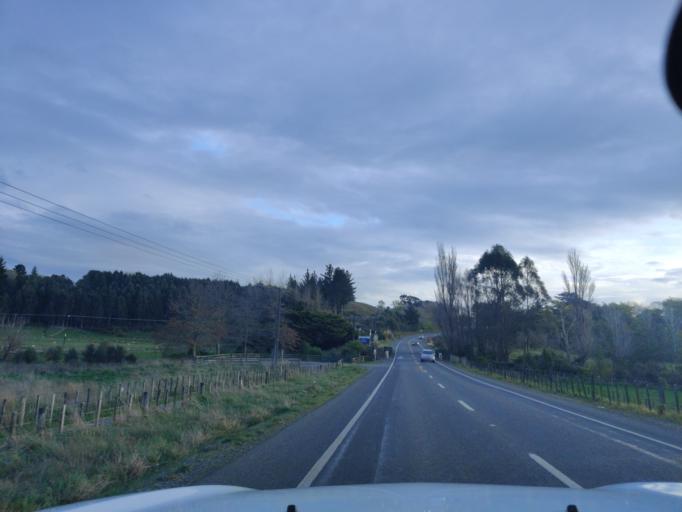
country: NZ
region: Manawatu-Wanganui
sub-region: Palmerston North City
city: Palmerston North
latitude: -40.3932
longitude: 175.6340
